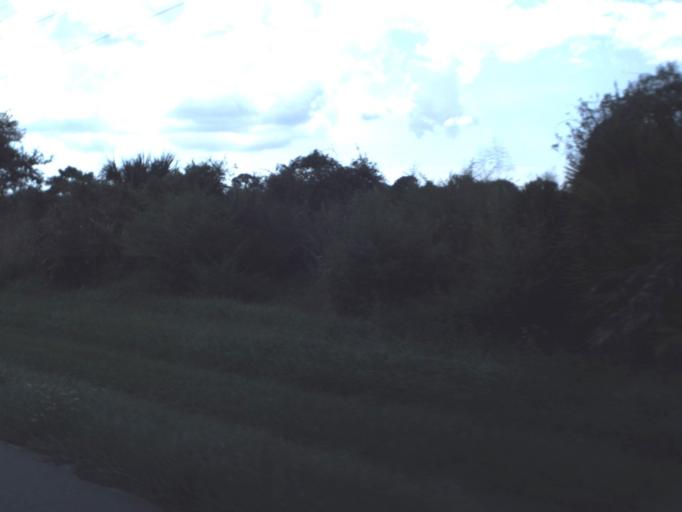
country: US
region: Florida
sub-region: Hillsborough County
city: Sun City Center
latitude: 27.5905
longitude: -82.3891
